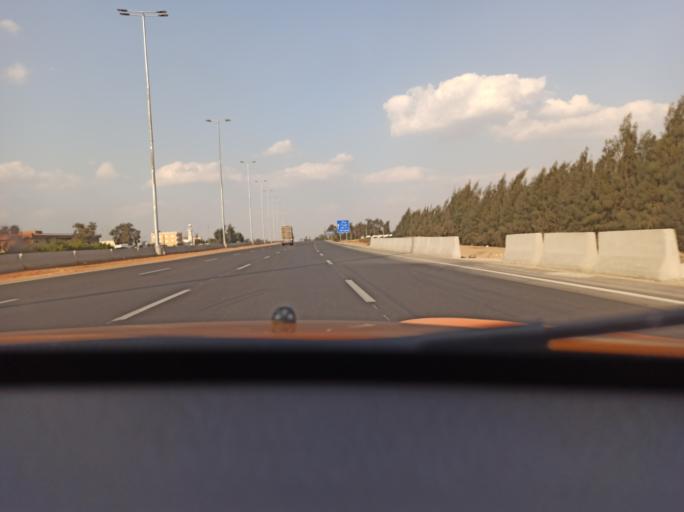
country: EG
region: Al Isma'iliyah
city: Ismailia
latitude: 30.5190
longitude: 32.1483
